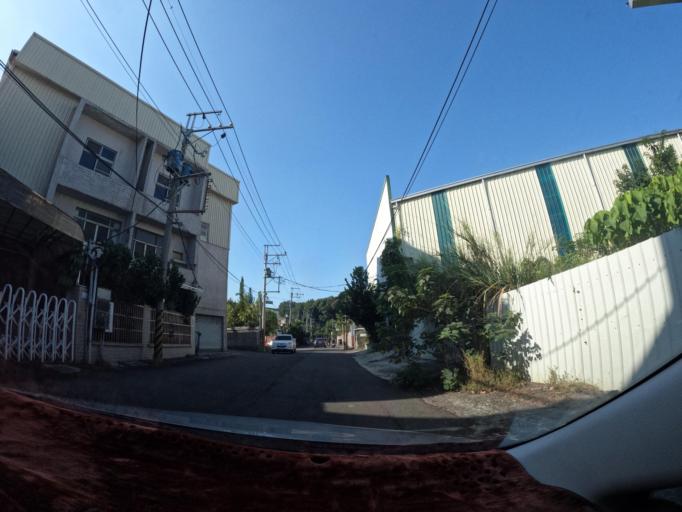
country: TW
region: Taiwan
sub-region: Tainan
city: Tainan
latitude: 23.0246
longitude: 120.2464
